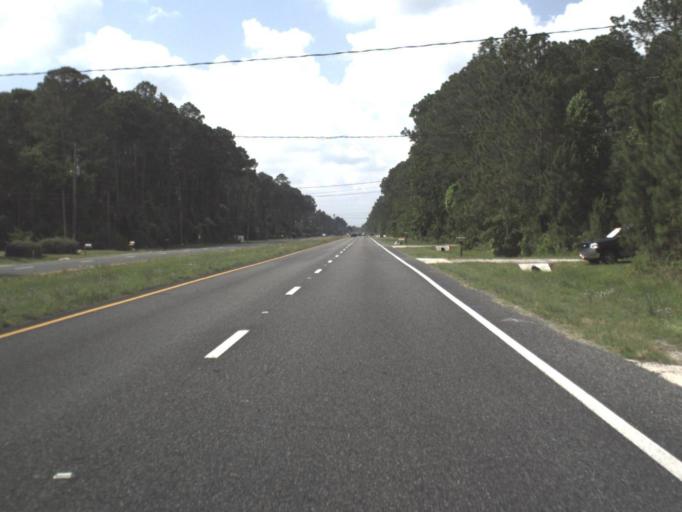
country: US
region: Florida
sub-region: Saint Johns County
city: Saint Augustine Shores
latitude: 29.7691
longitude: -81.3151
